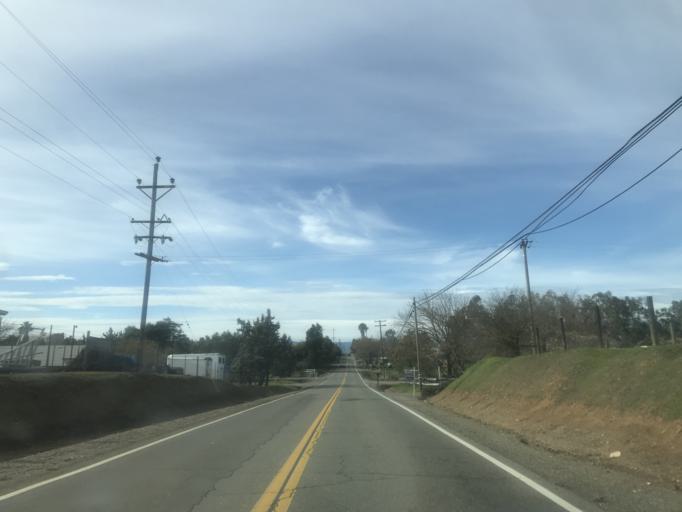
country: US
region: California
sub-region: Yolo County
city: Woodland
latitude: 38.6635
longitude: -121.8634
